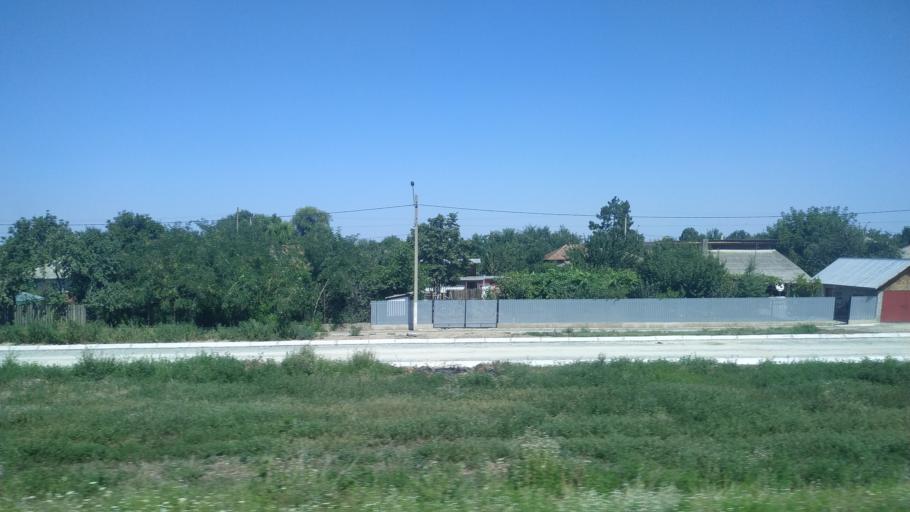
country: RO
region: Calarasi
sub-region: Comuna Perisoru
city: Perisoru
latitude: 44.4214
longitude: 27.6427
